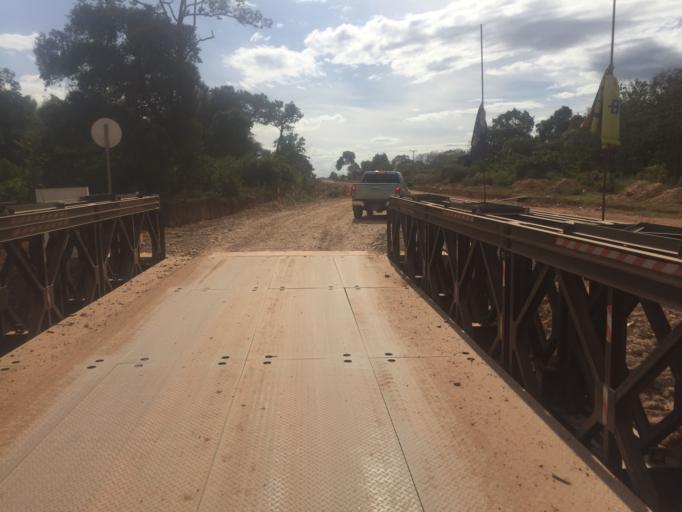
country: LA
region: Attapu
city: Attapu
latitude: 14.7960
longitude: 106.7531
